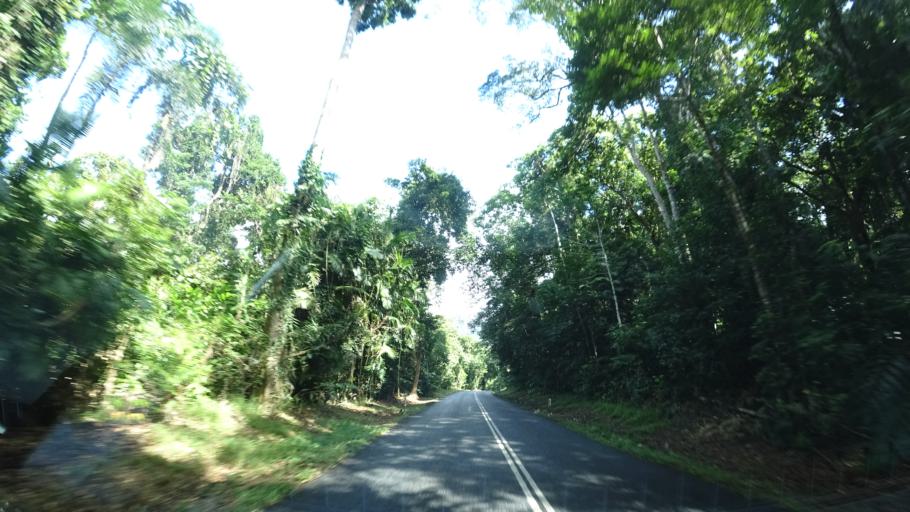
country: AU
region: Queensland
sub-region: Cairns
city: Port Douglas
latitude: -16.1380
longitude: 145.4368
